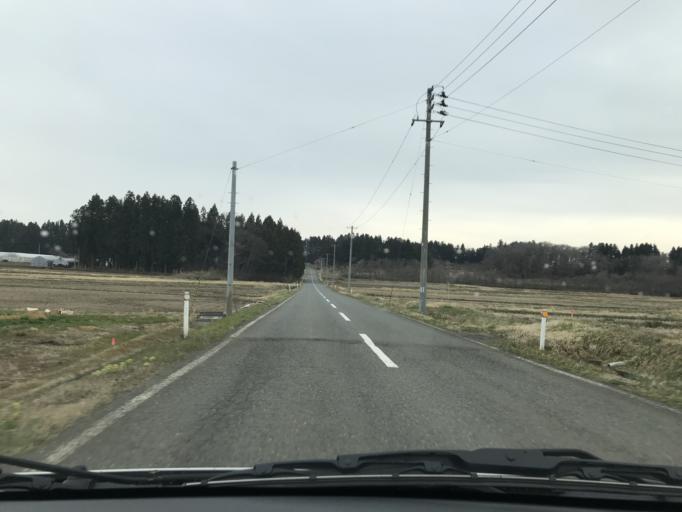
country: JP
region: Iwate
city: Mizusawa
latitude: 39.0960
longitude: 141.0691
